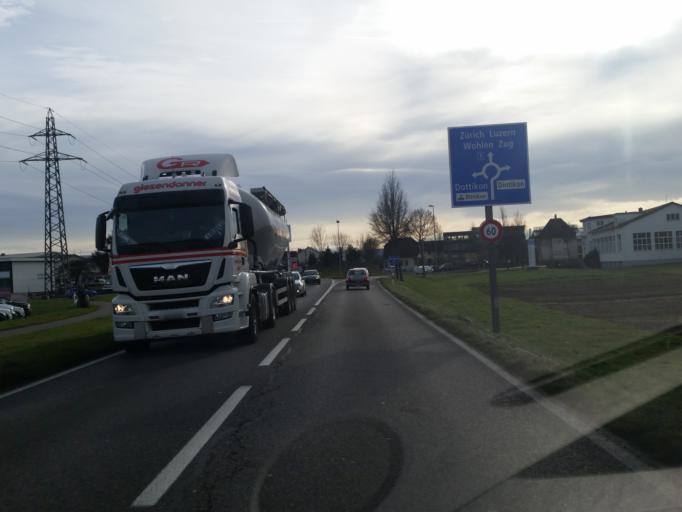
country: CH
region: Aargau
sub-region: Bezirk Bremgarten
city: Dottikon
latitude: 47.3711
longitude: 8.2301
